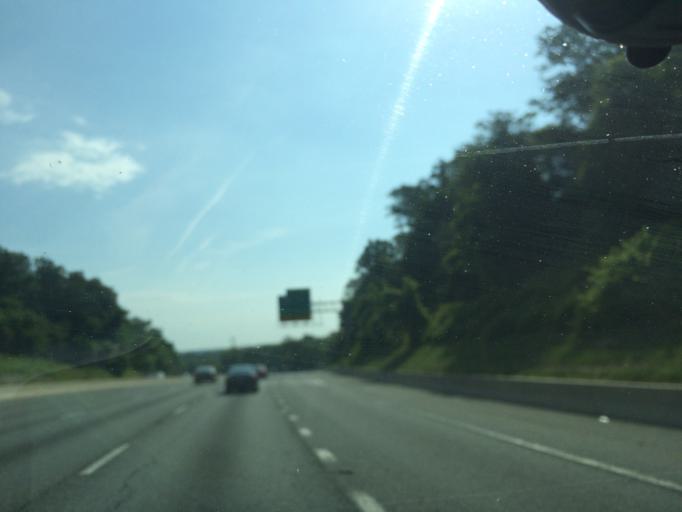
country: US
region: Maryland
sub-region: Baltimore County
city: Mays Chapel
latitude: 39.4046
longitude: -76.6740
